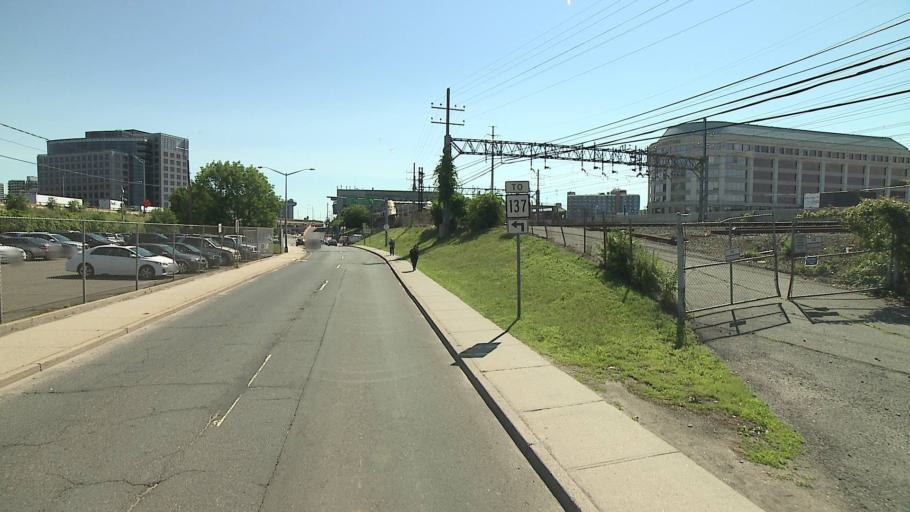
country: US
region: Connecticut
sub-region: Fairfield County
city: Stamford
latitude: 41.0462
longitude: -73.5445
